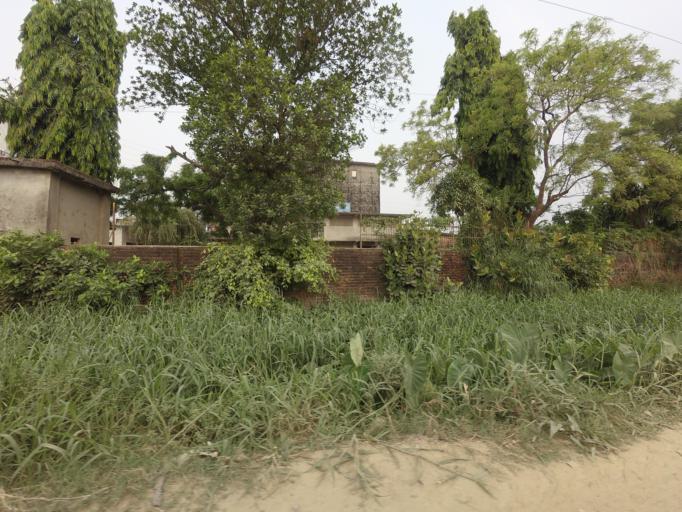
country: NP
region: Western Region
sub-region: Lumbini Zone
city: Bhairahawa
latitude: 27.5184
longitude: 83.4418
